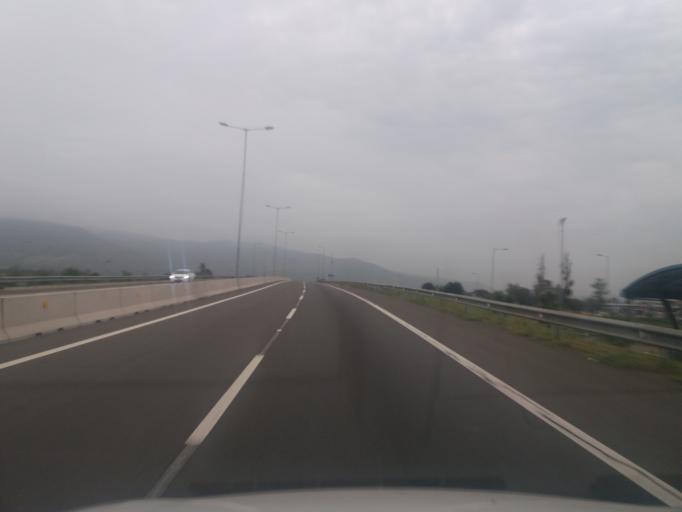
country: CL
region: Valparaiso
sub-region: Provincia de Quillota
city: Quillota
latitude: -32.8753
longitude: -71.2312
